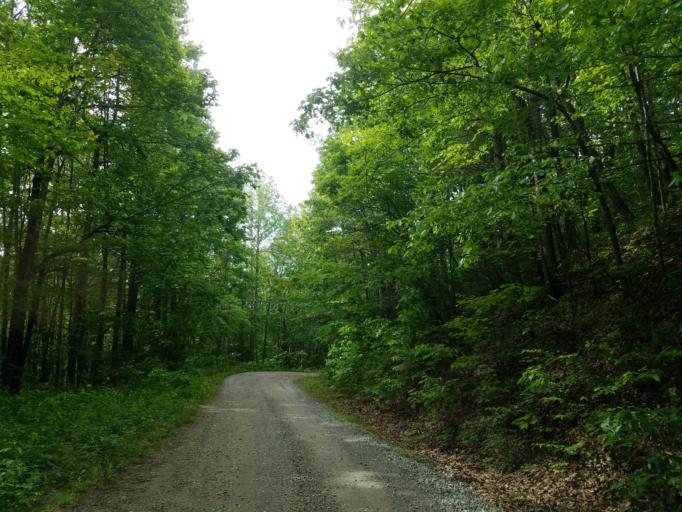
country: US
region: Georgia
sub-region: Union County
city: Blairsville
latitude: 34.7433
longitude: -83.9918
